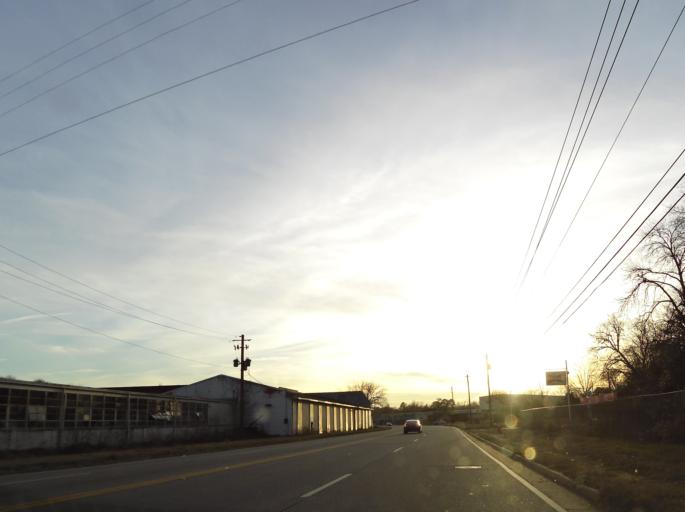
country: US
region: Georgia
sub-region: Bibb County
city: Macon
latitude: 32.7926
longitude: -83.6480
